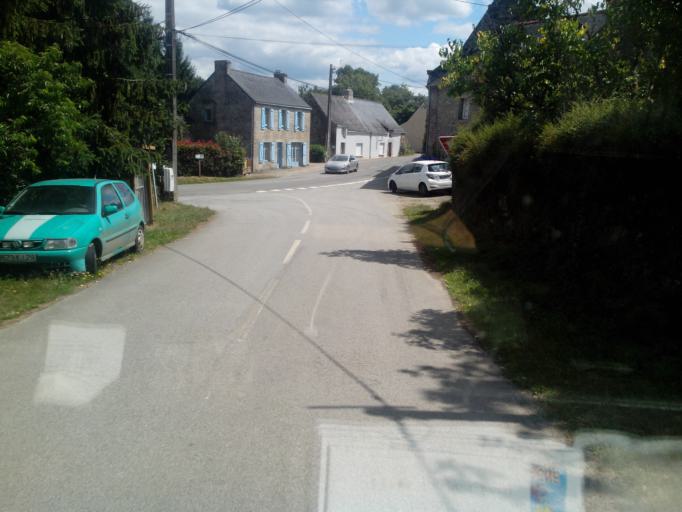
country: FR
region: Brittany
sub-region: Departement du Morbihan
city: Plumelec
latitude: 47.8214
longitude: -2.6563
